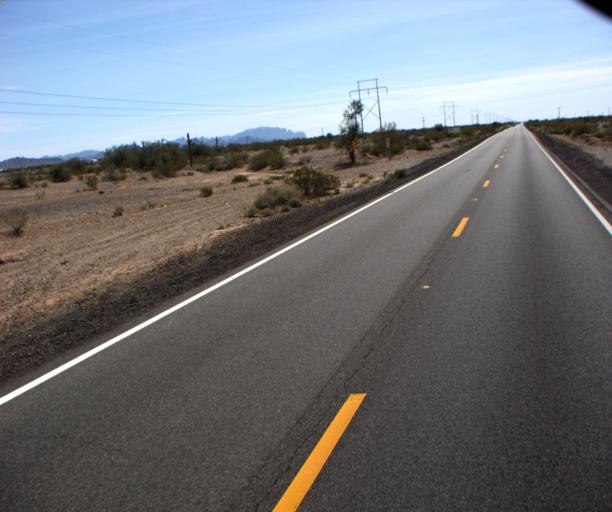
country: US
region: Arizona
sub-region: La Paz County
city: Quartzsite
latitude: 33.6212
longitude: -114.2171
